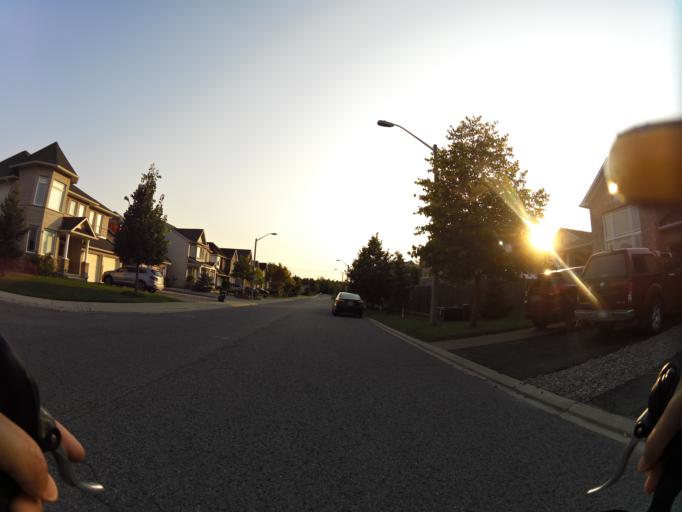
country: CA
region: Ontario
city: Bells Corners
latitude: 45.3515
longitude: -75.9467
